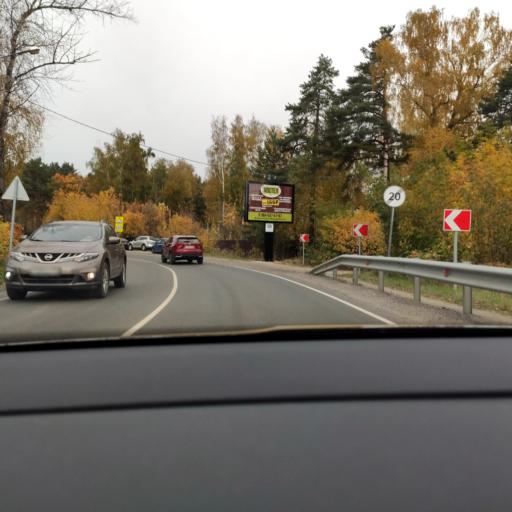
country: RU
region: Moskovskaya
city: Ivanteyevka
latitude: 55.9859
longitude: 37.9306
